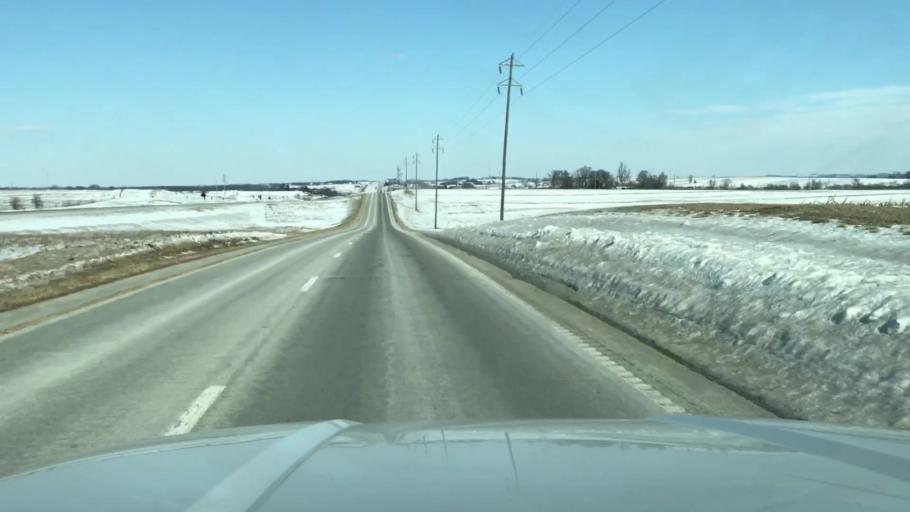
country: US
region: Missouri
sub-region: Andrew County
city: Savannah
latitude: 40.1231
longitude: -94.8696
